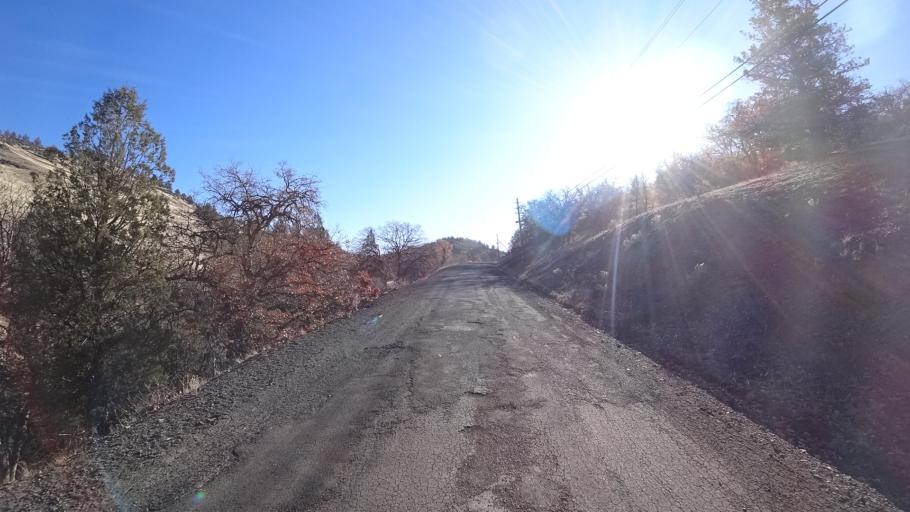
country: US
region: California
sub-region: Siskiyou County
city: Montague
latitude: 41.9161
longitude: -122.4457
